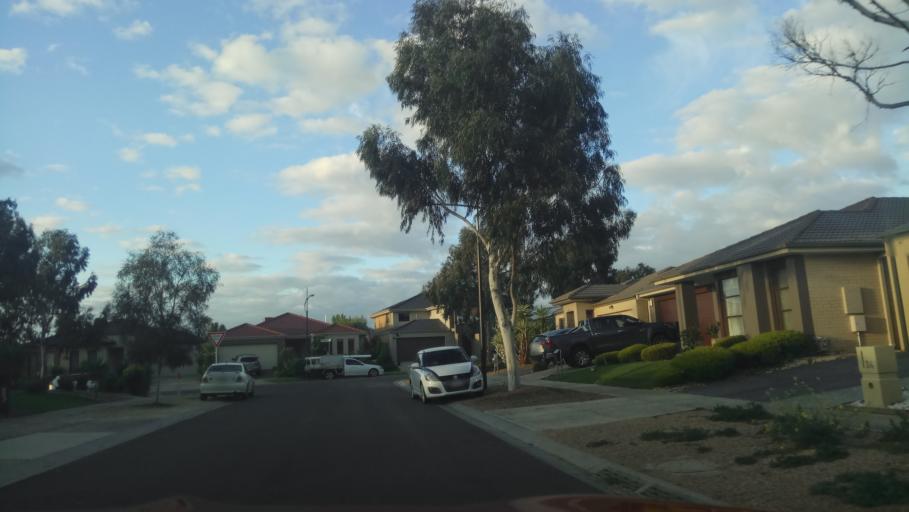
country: AU
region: Victoria
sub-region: Wyndham
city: Point Cook
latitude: -37.9118
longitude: 144.7366
